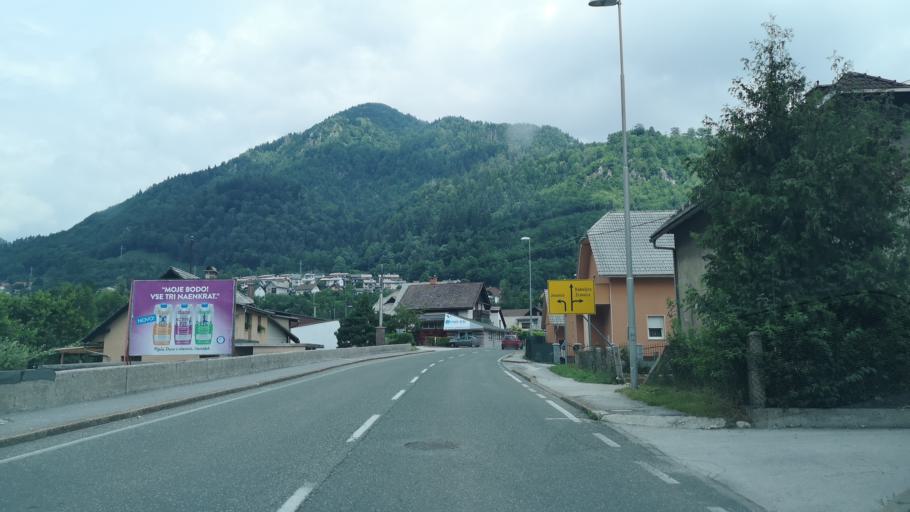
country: SI
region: Jesenice
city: Slovenski Javornik
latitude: 46.4255
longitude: 14.0816
